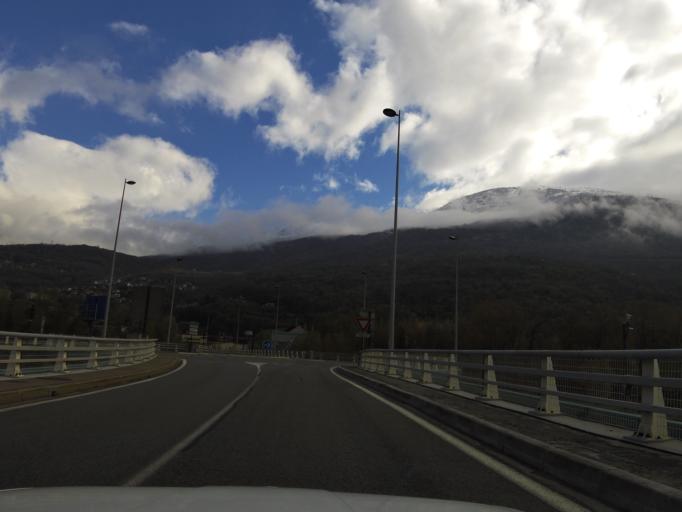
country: FR
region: Rhone-Alpes
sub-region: Departement de la Savoie
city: Saint-Michel-de-Maurienne
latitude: 45.2181
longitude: 6.4618
